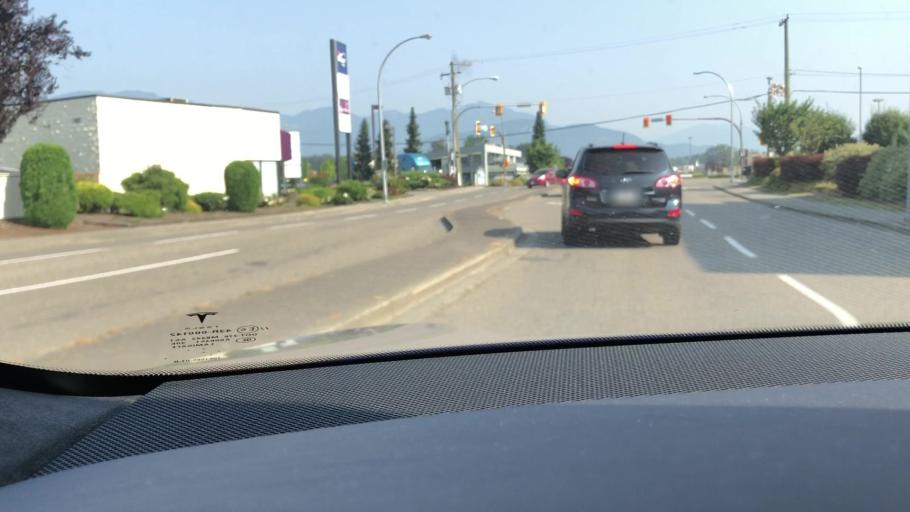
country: CA
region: British Columbia
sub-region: Fraser Valley Regional District
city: Chilliwack
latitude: 49.1404
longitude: -121.9668
